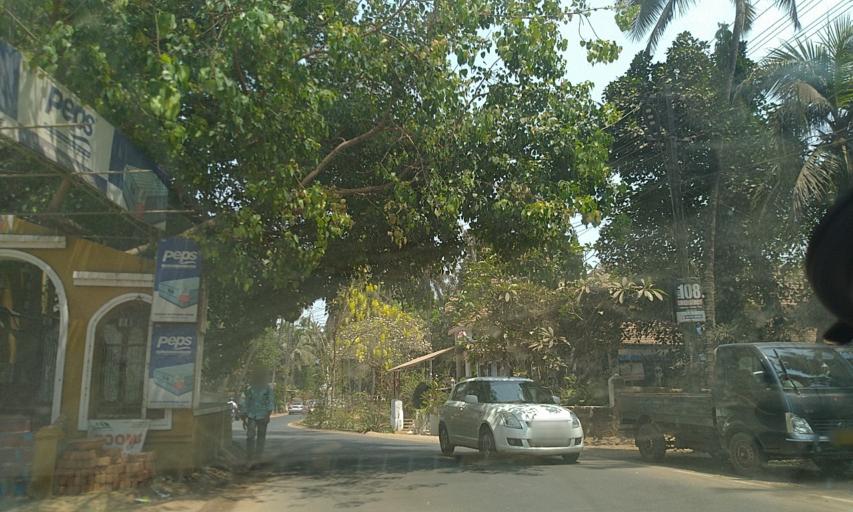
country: IN
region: Goa
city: Calangute
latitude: 15.5476
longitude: 73.7665
